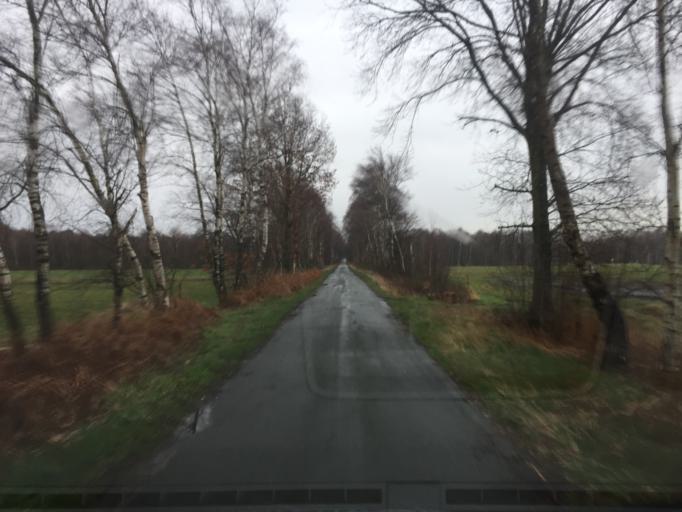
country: DE
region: Lower Saxony
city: Kirchdorf
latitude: 52.6188
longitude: 8.8978
